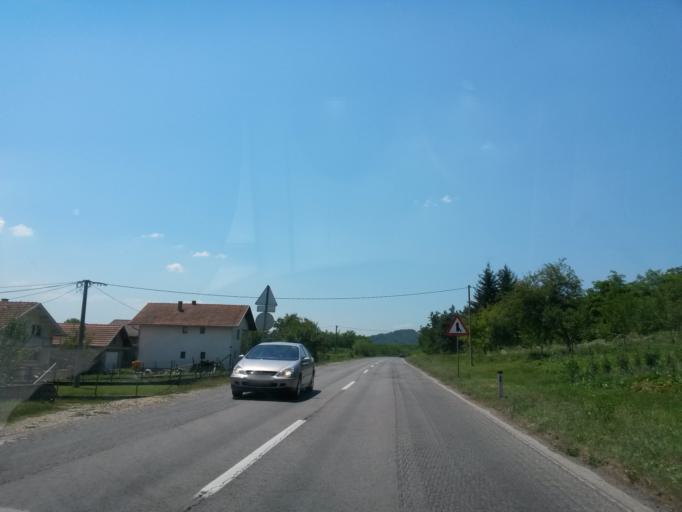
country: BA
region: Republika Srpska
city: Doboj
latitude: 44.8250
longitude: 18.0618
